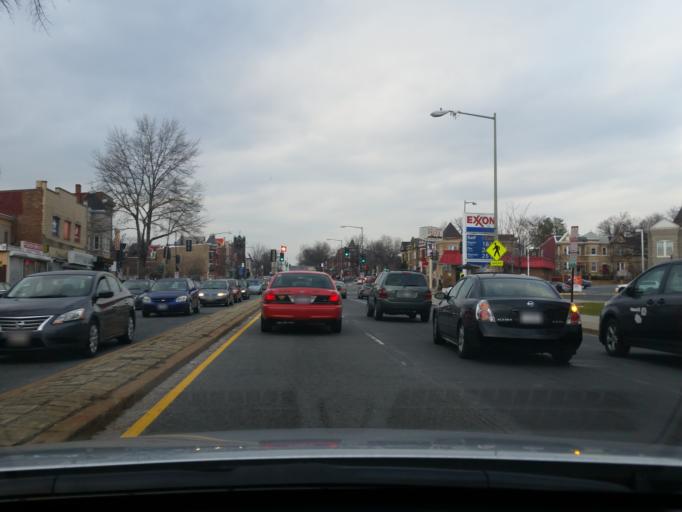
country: US
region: Washington, D.C.
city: Washington, D.C.
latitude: 38.9100
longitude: -77.0091
